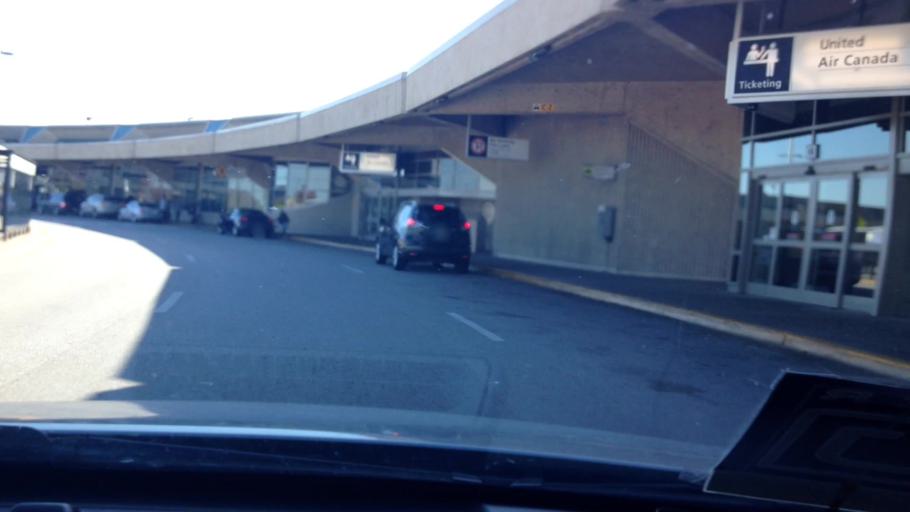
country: US
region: Missouri
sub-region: Platte County
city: Weatherby Lake
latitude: 39.2941
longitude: -94.7149
